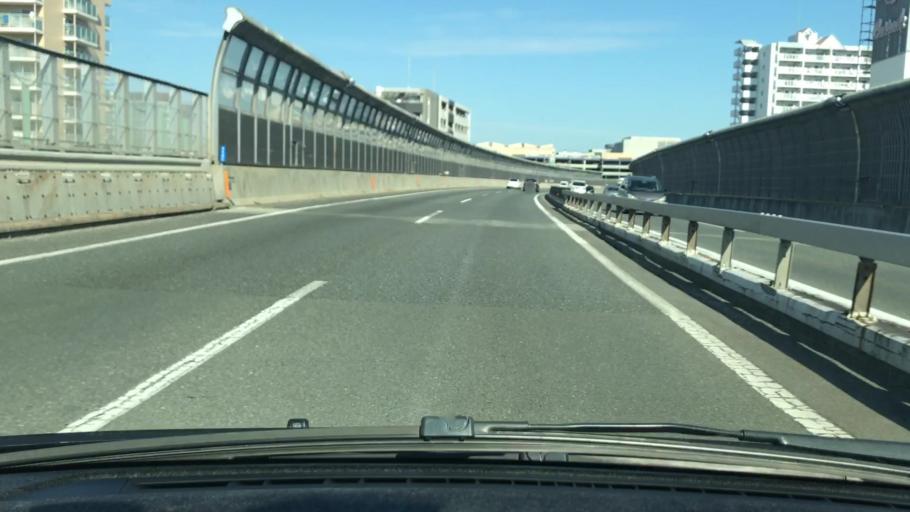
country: JP
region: Hyogo
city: Nishinomiya-hama
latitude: 34.7390
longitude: 135.3595
